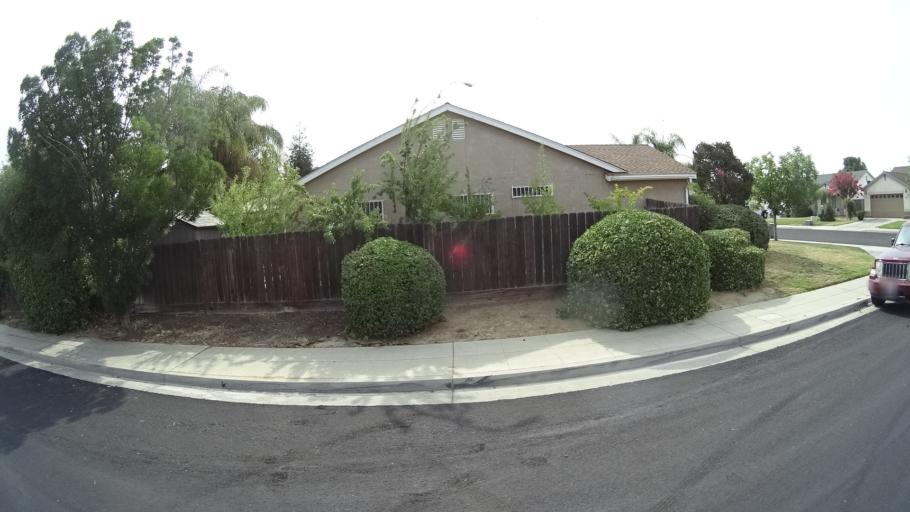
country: US
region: California
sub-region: Fresno County
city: West Park
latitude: 36.7695
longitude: -119.8655
